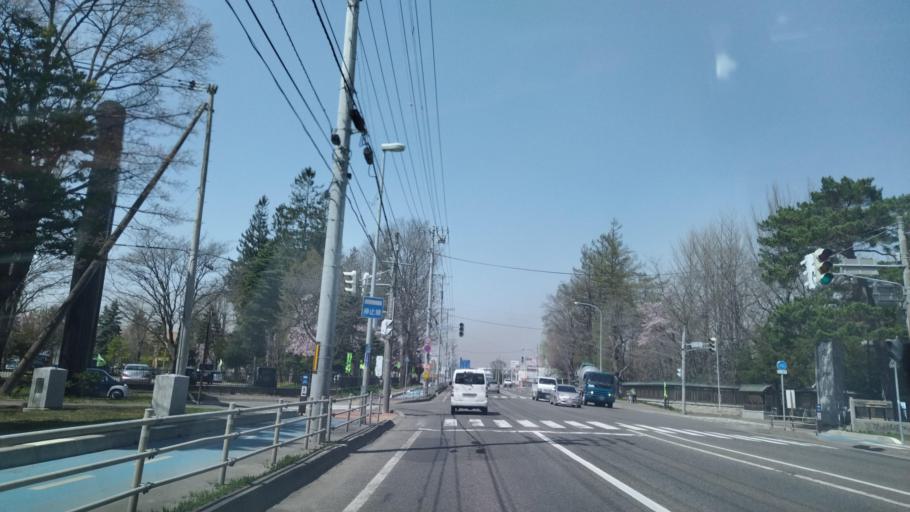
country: JP
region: Hokkaido
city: Obihiro
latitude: 42.9304
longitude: 143.2095
